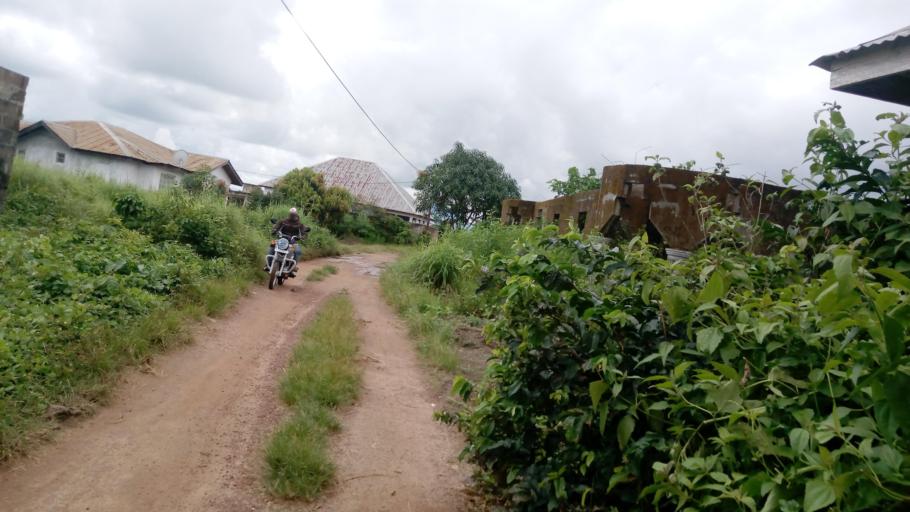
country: SL
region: Northern Province
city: Makeni
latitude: 8.9013
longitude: -12.0245
